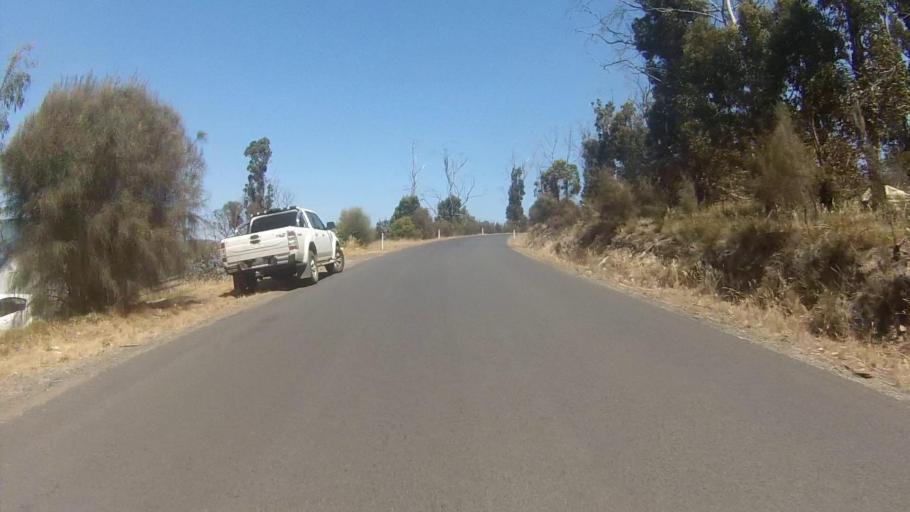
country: AU
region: Tasmania
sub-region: Sorell
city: Sorell
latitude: -42.8727
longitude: 147.8267
